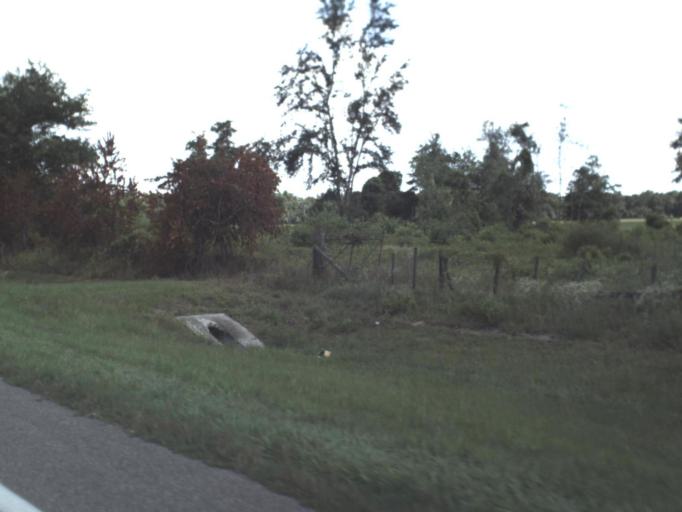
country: US
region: Florida
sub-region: Lafayette County
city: Mayo
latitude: 29.9929
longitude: -83.0106
